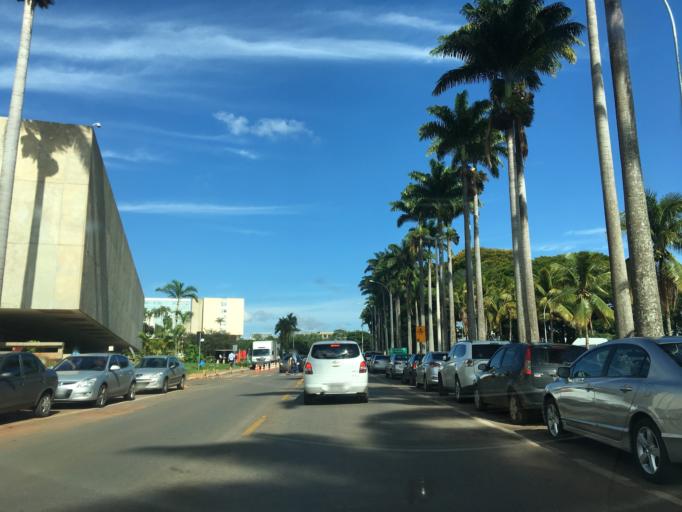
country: BR
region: Federal District
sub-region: Brasilia
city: Brasilia
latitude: -15.7978
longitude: -47.8629
